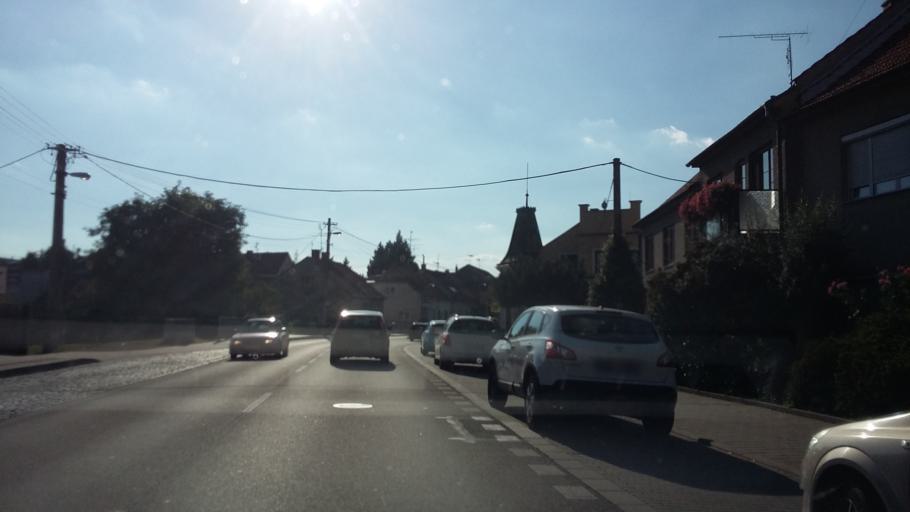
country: CZ
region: South Moravian
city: Ostopovice
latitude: 49.1736
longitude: 16.5317
